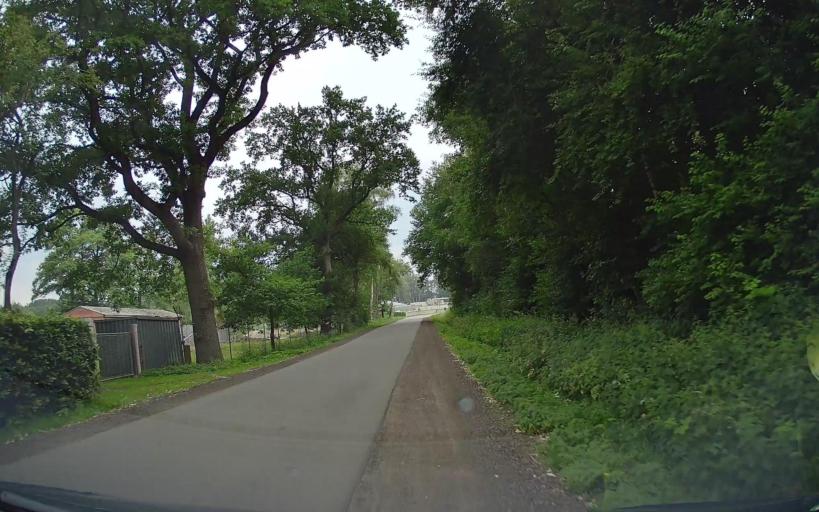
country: DE
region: Lower Saxony
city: Friesoythe
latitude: 53.0350
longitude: 7.8390
